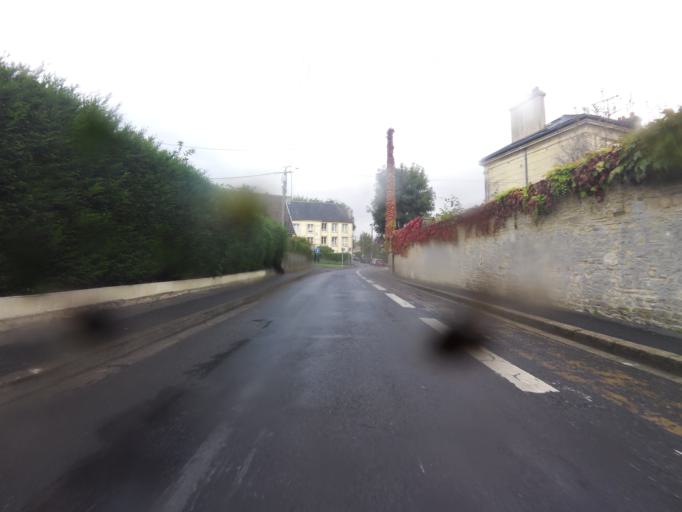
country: FR
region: Lower Normandy
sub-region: Departement du Calvados
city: Caen
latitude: 49.1930
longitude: -0.3570
